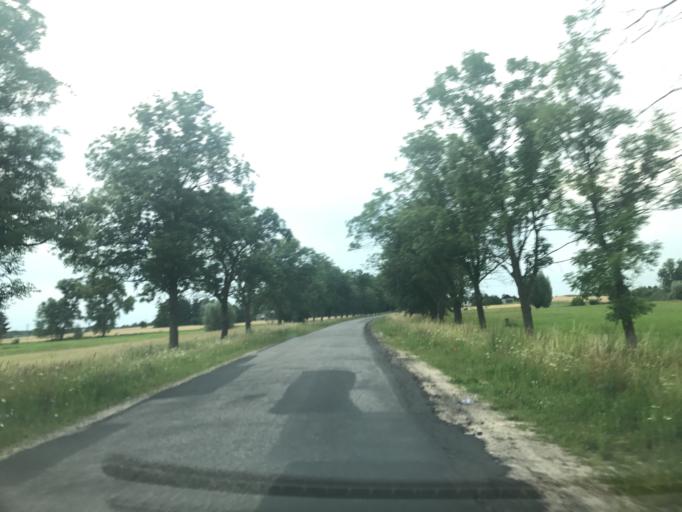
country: PL
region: Kujawsko-Pomorskie
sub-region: Powiat lipnowski
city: Lipno
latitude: 52.7840
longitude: 19.2093
